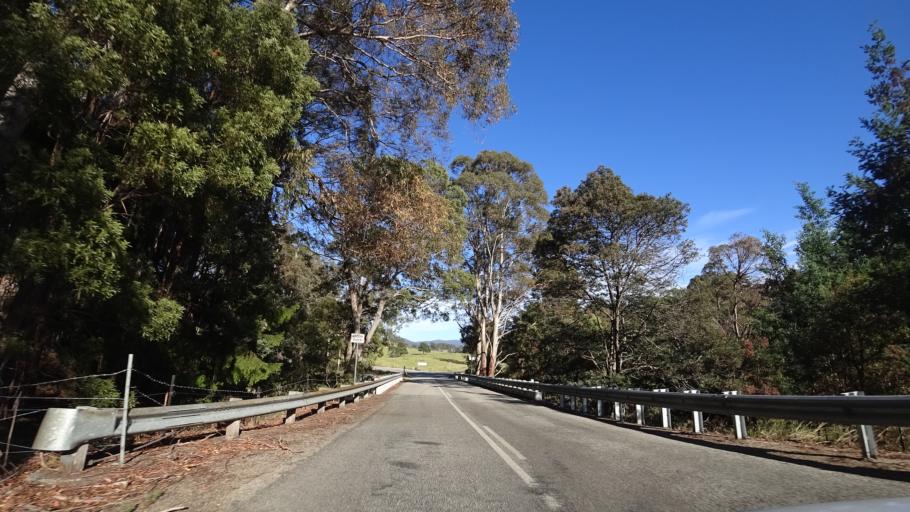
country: AU
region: Tasmania
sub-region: Break O'Day
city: St Helens
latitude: -41.2552
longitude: 148.0835
